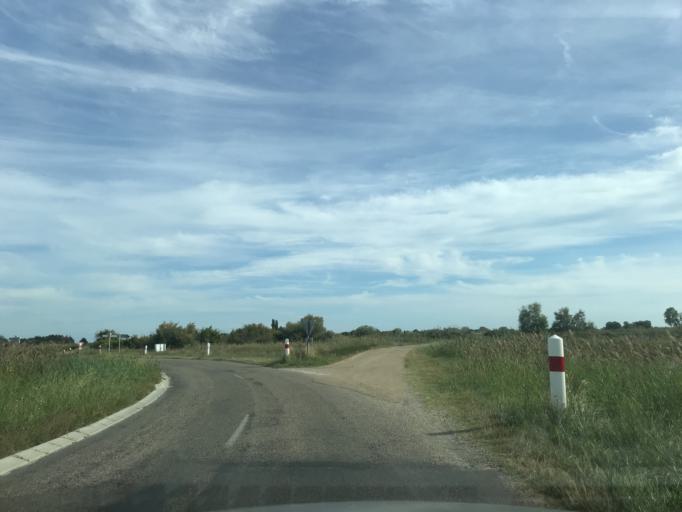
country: FR
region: Provence-Alpes-Cote d'Azur
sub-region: Departement des Bouches-du-Rhone
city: Saintes-Maries-de-la-Mer
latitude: 43.5255
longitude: 4.3776
